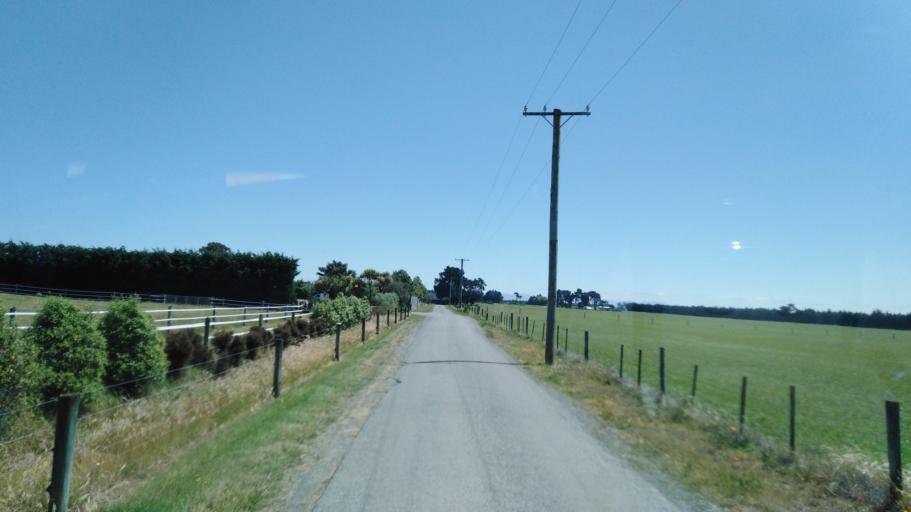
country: NZ
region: Canterbury
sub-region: Selwyn District
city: Rolleston
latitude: -43.5642
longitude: 172.4385
